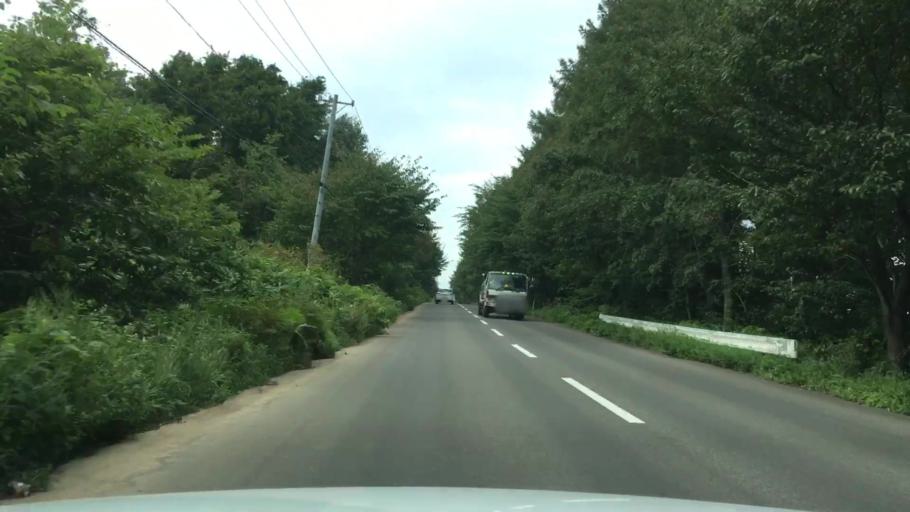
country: JP
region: Aomori
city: Shimokizukuri
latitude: 40.7151
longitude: 140.3176
